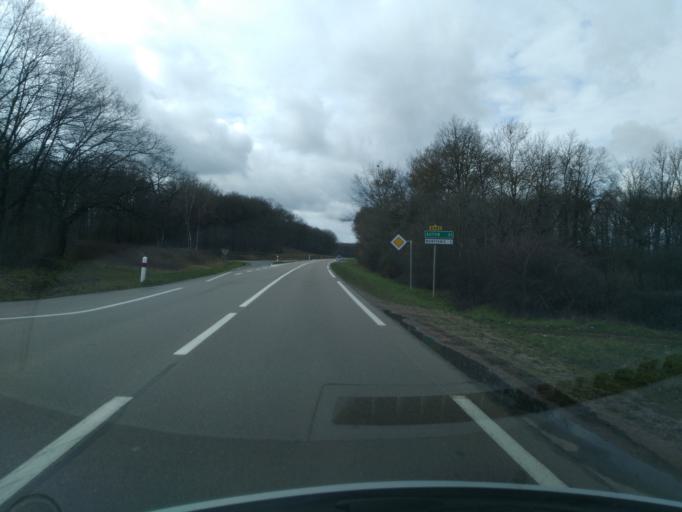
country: FR
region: Bourgogne
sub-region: Departement de Saone-et-Loire
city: Torcy
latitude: 46.7669
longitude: 4.4407
